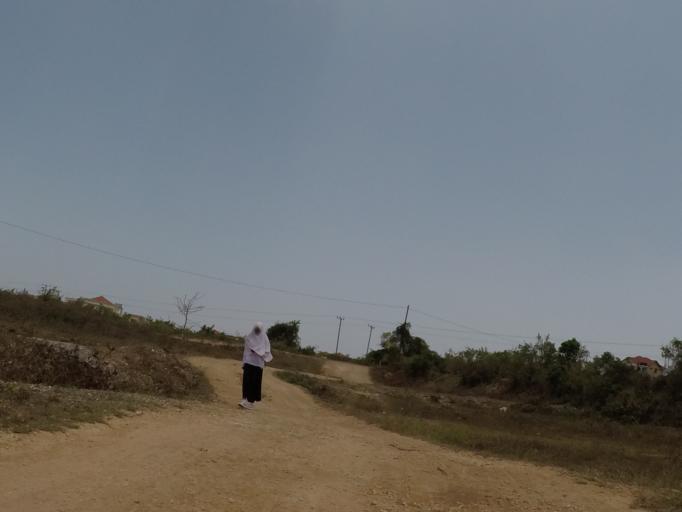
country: TZ
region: Zanzibar Central/South
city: Koani
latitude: -6.1934
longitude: 39.3089
